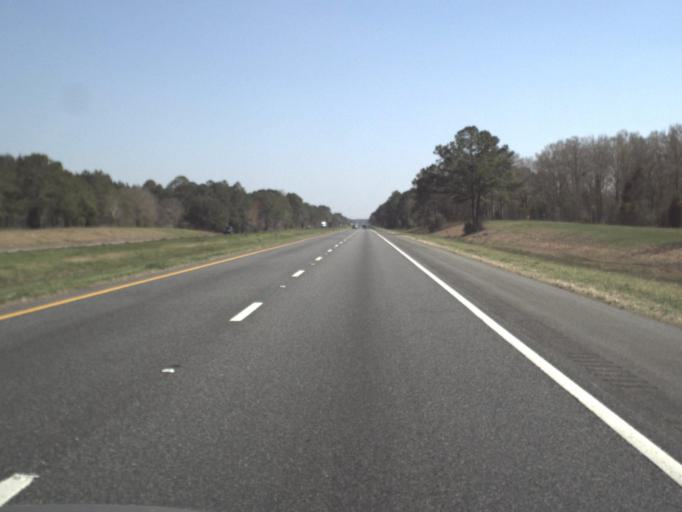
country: US
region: Florida
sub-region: Jackson County
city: Marianna
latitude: 30.7117
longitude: -85.1555
